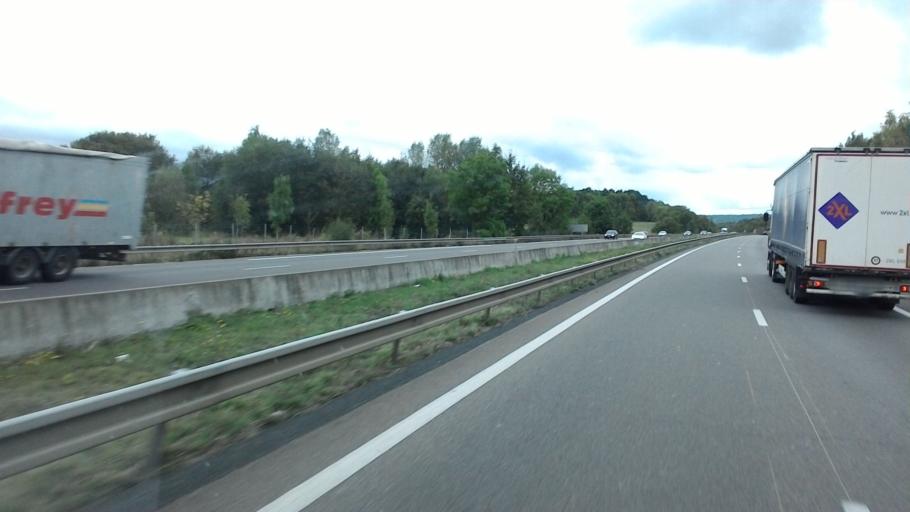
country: FR
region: Lorraine
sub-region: Departement de la Moselle
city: Augny
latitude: 49.0616
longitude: 6.1114
